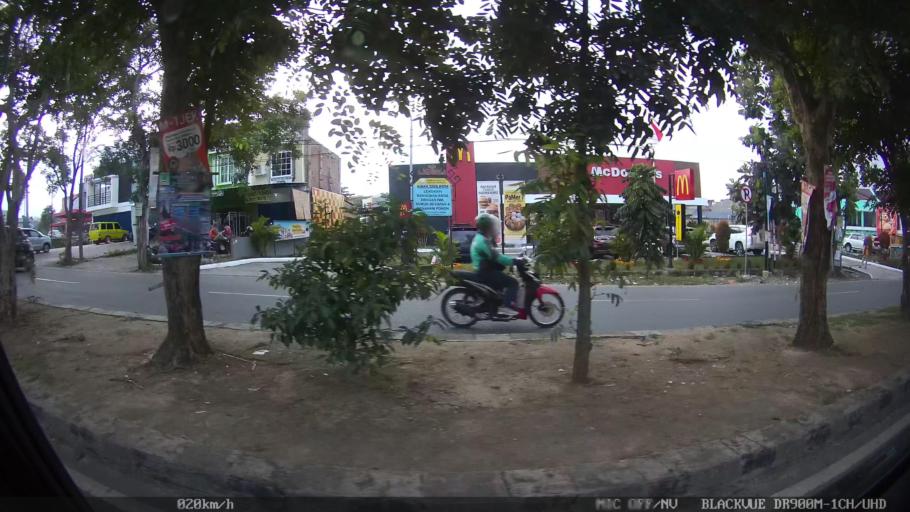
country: ID
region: Lampung
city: Kedaton
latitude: -5.3981
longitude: 105.2124
